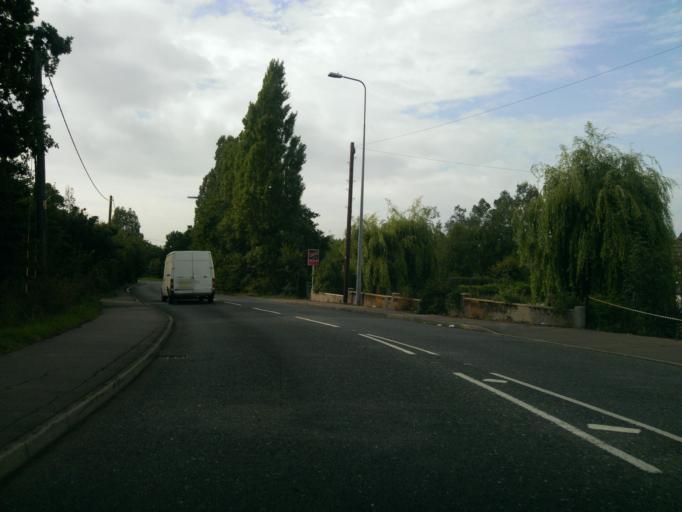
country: GB
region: England
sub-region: Essex
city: Little Clacton
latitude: 51.8200
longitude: 1.1417
